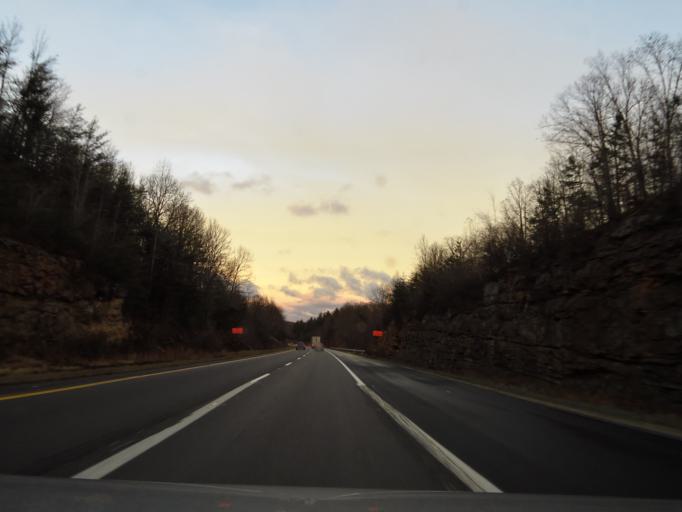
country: US
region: Tennessee
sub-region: Campbell County
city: Jacksboro
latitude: 36.4472
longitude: -84.2708
